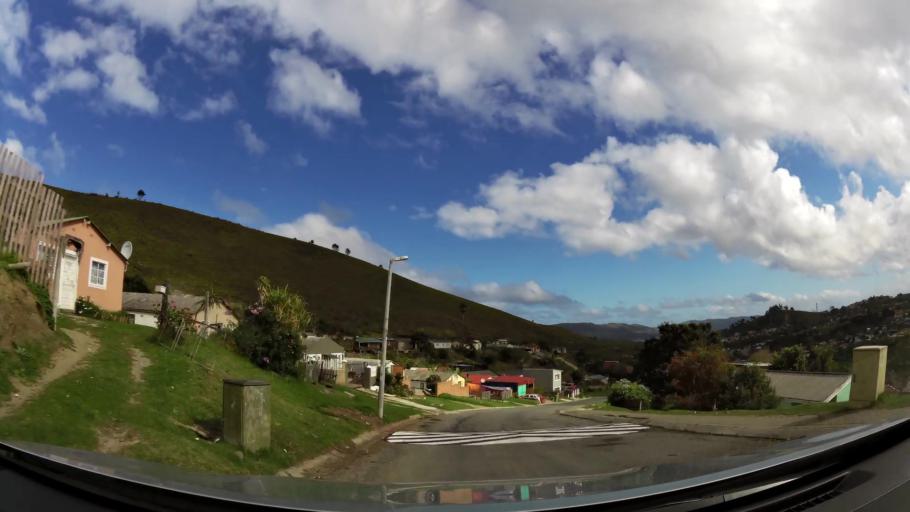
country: ZA
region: Western Cape
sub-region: Eden District Municipality
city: Knysna
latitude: -34.0542
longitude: 23.1040
